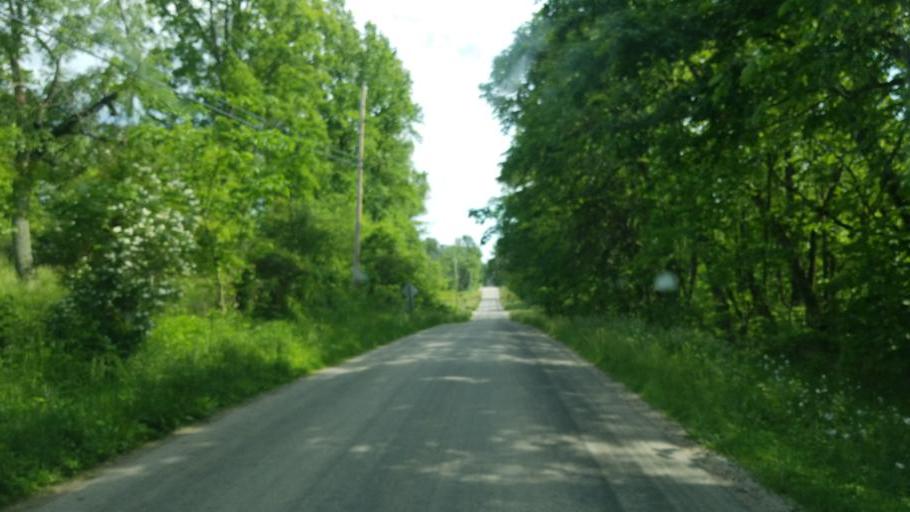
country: US
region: Ohio
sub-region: Huron County
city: Greenwich
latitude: 40.9162
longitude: -82.5327
